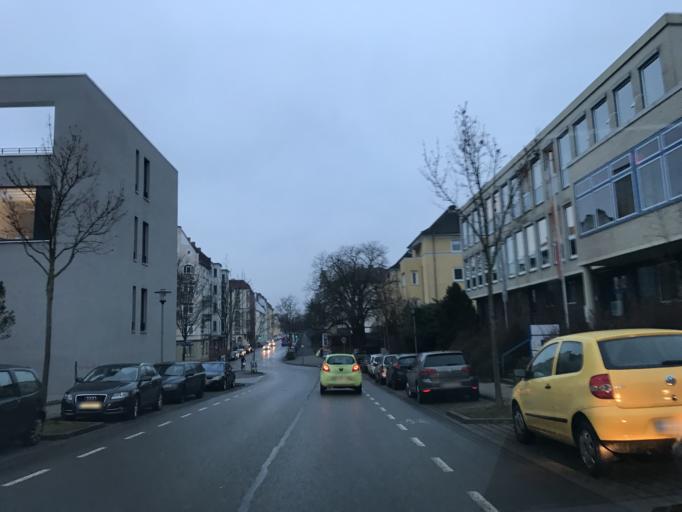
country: DE
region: Hesse
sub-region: Regierungsbezirk Kassel
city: Kassel
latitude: 51.3180
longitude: 9.4710
